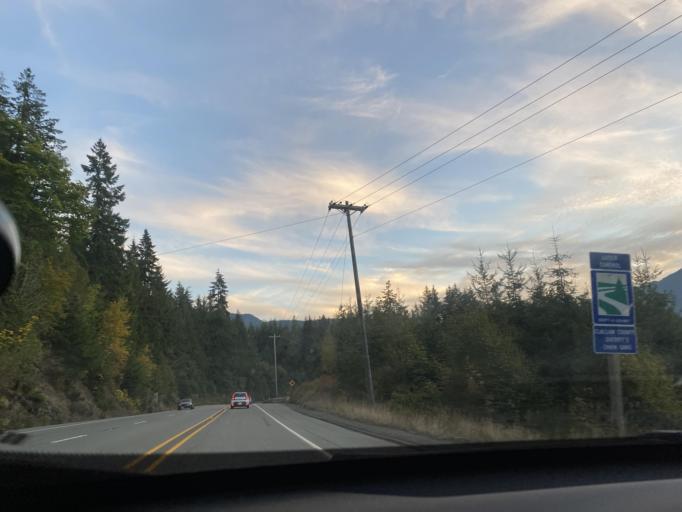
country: US
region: Washington
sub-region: Clallam County
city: Port Angeles
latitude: 48.0837
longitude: -123.5583
